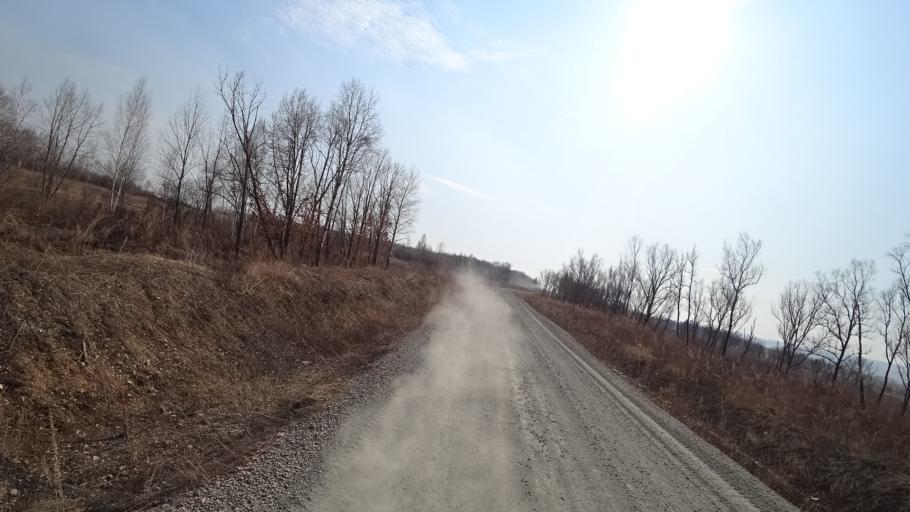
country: RU
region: Amur
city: Novobureyskiy
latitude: 49.8250
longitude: 129.9868
